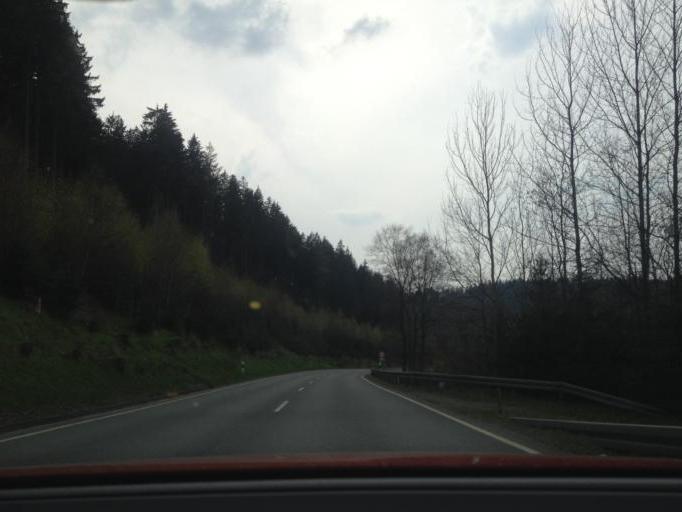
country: DE
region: Bavaria
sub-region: Upper Franconia
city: Bischofsgrun
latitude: 50.0473
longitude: 11.7492
